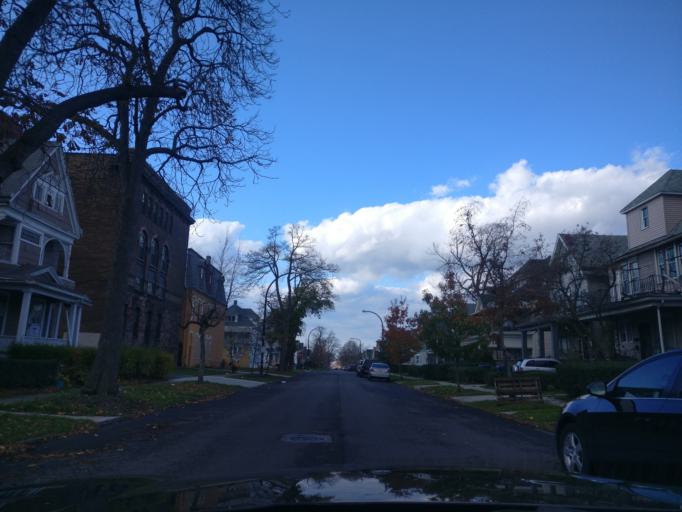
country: US
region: New York
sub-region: Erie County
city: Buffalo
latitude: 42.9075
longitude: -78.8963
